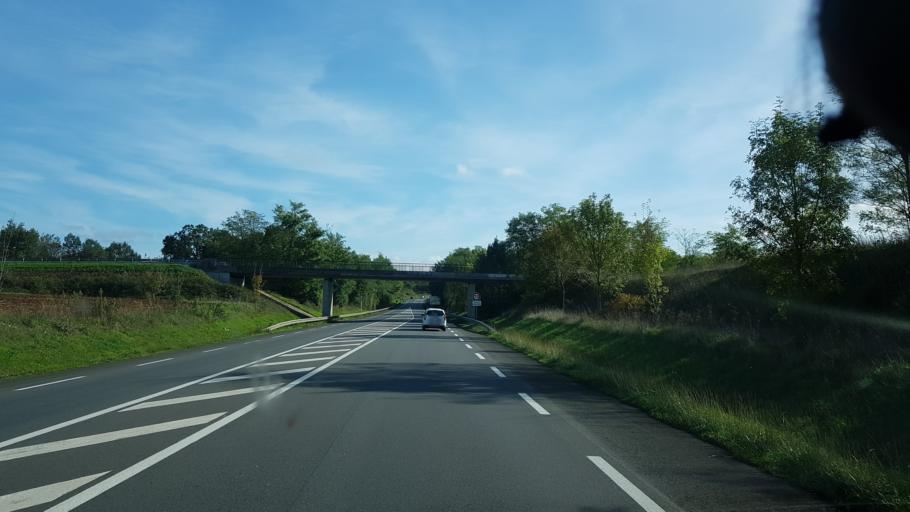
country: FR
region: Poitou-Charentes
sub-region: Departement de la Charente
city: Chasseneuil-sur-Bonnieure
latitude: 45.8360
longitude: 0.4652
